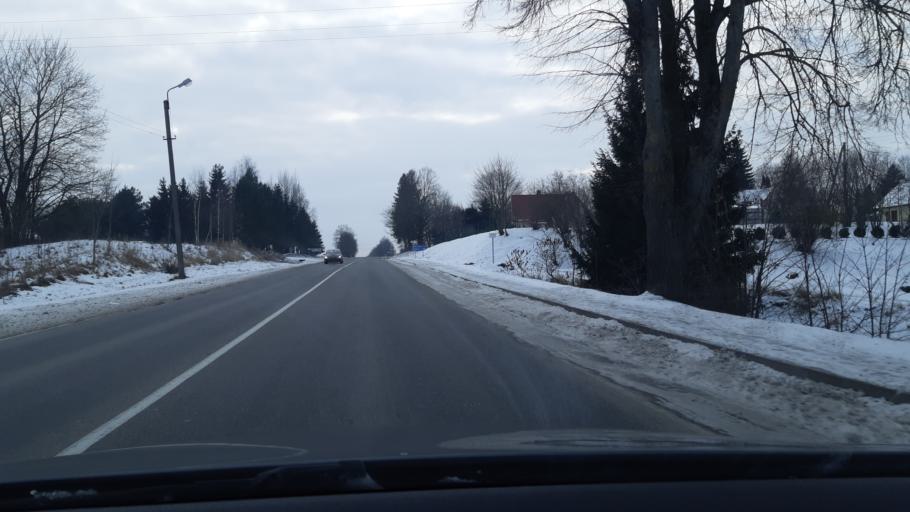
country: LT
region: Kauno apskritis
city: Kedainiai
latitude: 55.2412
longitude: 23.8312
